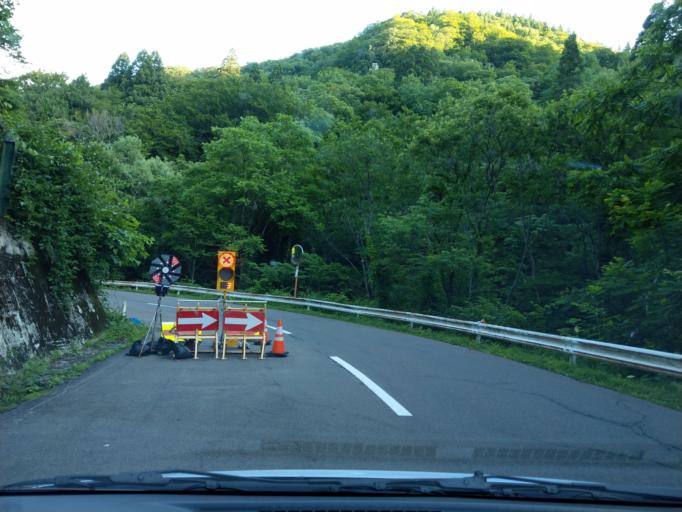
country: JP
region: Akita
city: Kakunodatemachi
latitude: 39.8766
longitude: 140.4788
